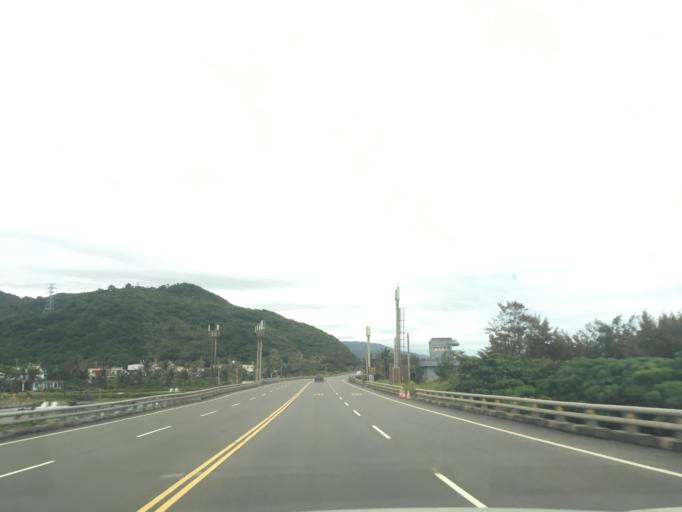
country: TW
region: Taiwan
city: Hengchun
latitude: 22.3060
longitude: 120.8899
